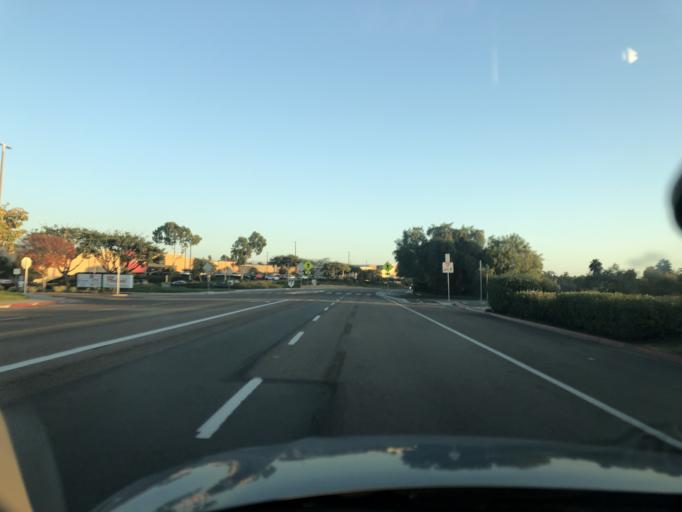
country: US
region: California
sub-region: San Diego County
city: Chula Vista
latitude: 32.6569
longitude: -117.0689
